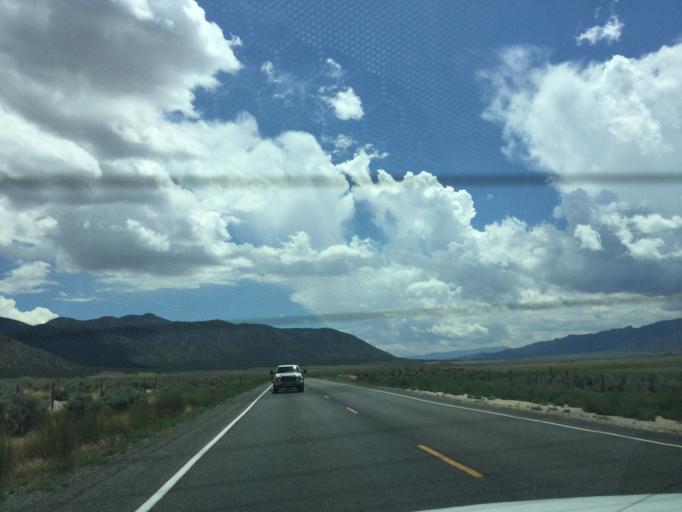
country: US
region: Utah
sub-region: Sevier County
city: Aurora
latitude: 39.1131
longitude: -112.0451
